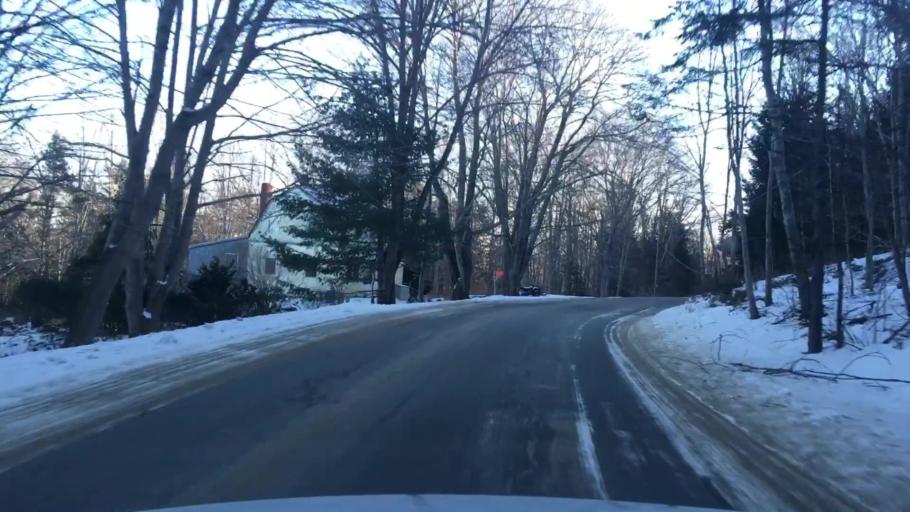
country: US
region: Maine
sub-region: Hancock County
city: Castine
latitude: 44.3476
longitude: -68.7824
